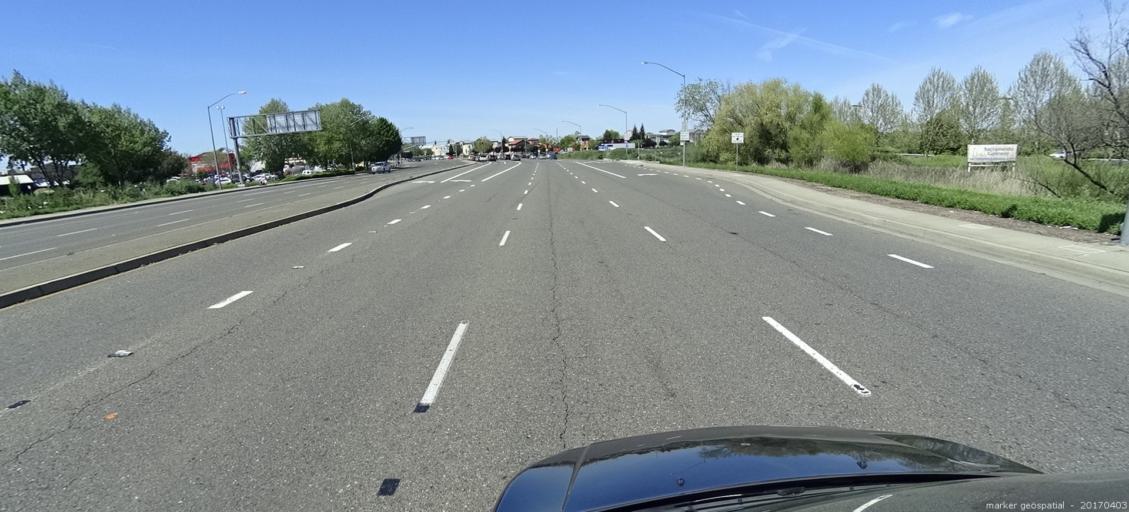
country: US
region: California
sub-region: Sacramento County
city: Sacramento
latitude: 38.6359
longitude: -121.5022
